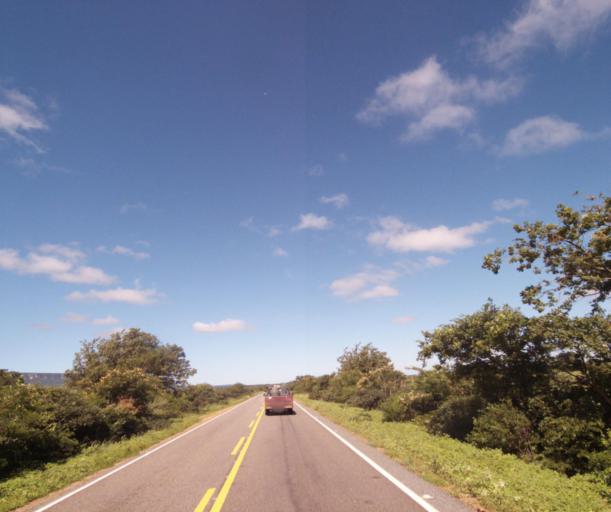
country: BR
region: Bahia
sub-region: Palmas De Monte Alto
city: Palmas de Monte Alto
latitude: -14.2416
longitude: -43.0636
